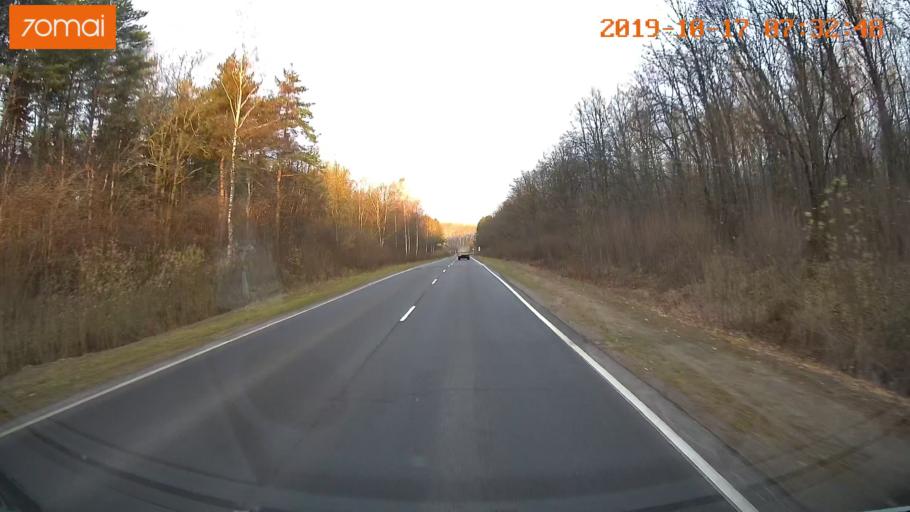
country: RU
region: Ivanovo
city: Gavrilov Posad
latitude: 56.3996
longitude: 39.9673
